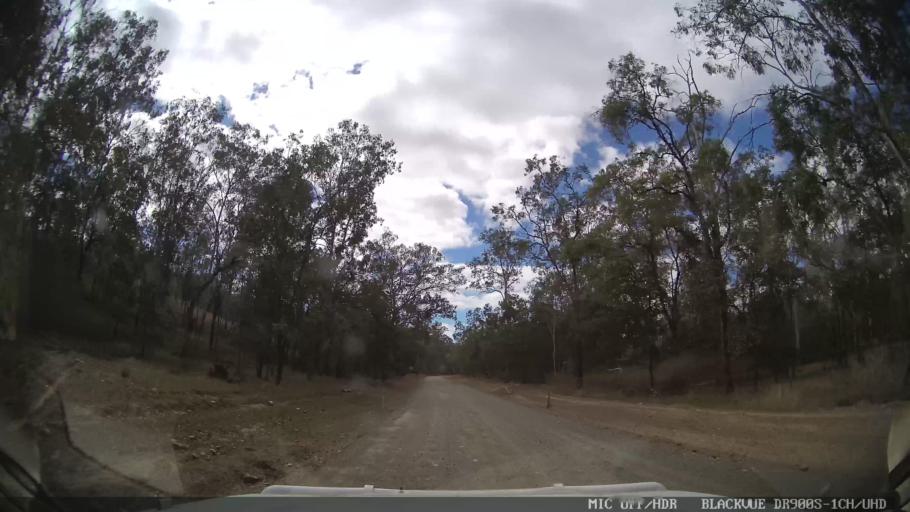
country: AU
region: Queensland
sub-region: Gladstone
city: Toolooa
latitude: -24.5494
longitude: 151.3426
